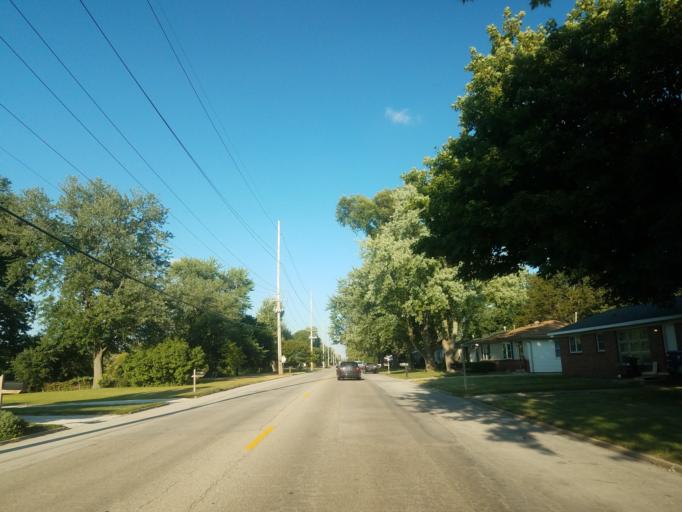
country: US
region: Illinois
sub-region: McLean County
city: Bloomington
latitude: 40.4667
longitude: -88.9717
